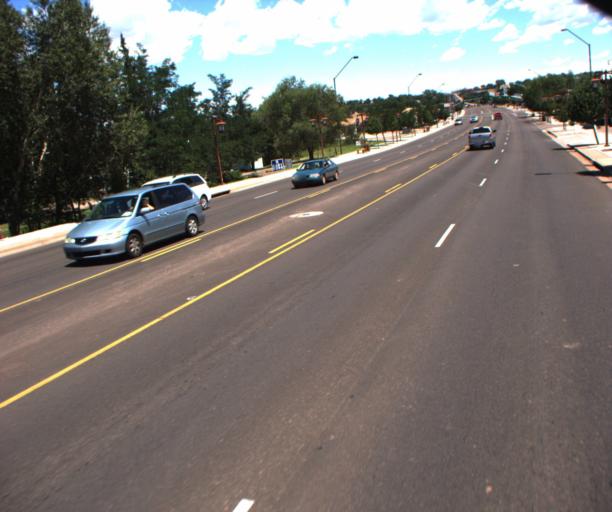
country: US
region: Arizona
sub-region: Navajo County
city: Show Low
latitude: 34.2530
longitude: -110.0348
